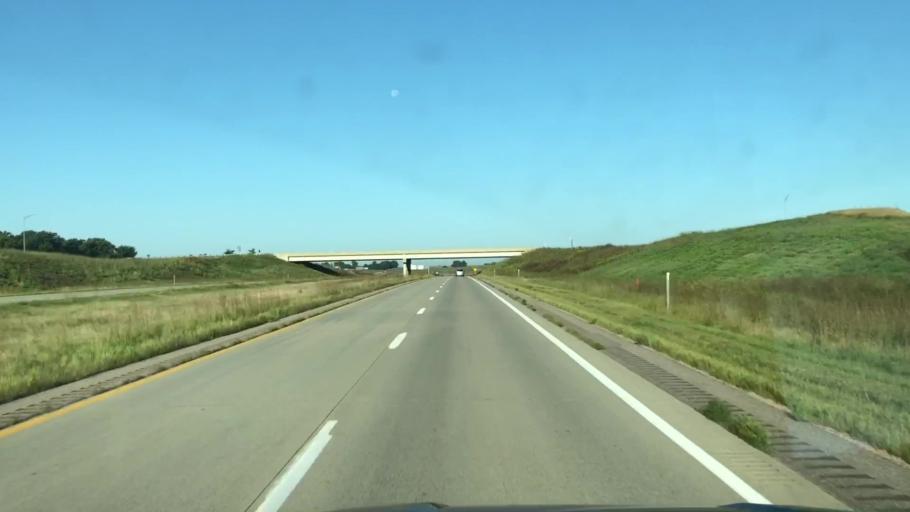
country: US
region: Iowa
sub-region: Plymouth County
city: Le Mars
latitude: 42.8186
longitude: -96.1717
